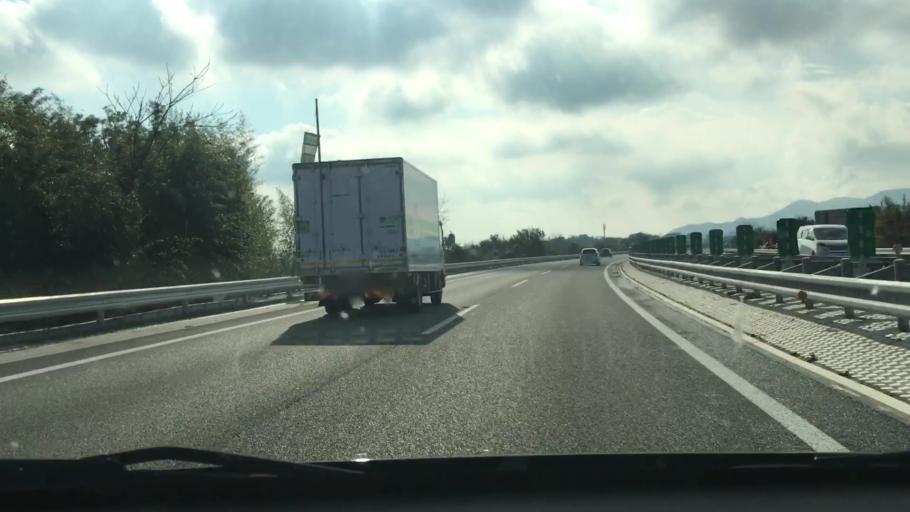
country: JP
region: Kumamoto
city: Uto
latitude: 32.7160
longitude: 130.7675
